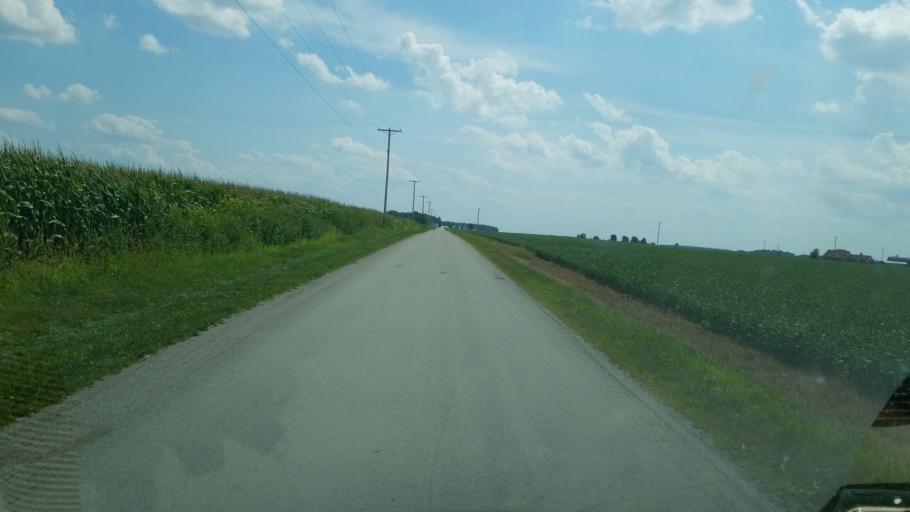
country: US
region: Ohio
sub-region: Hardin County
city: Forest
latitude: 40.7883
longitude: -83.4678
